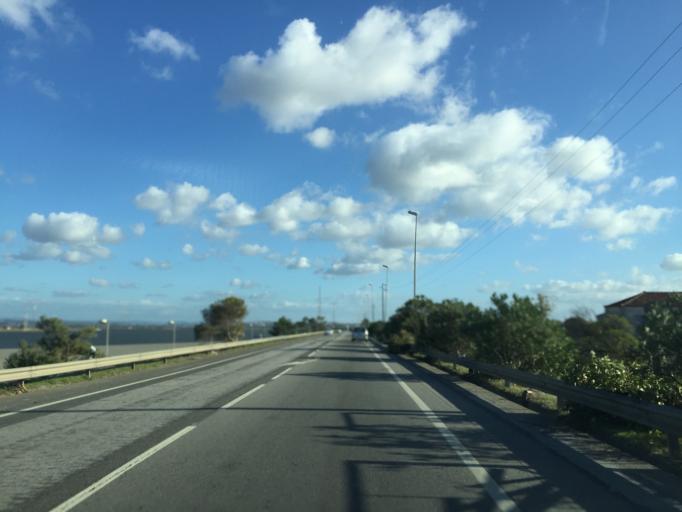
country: PT
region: Coimbra
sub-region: Figueira da Foz
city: Figueira da Foz
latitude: 40.1315
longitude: -8.8544
